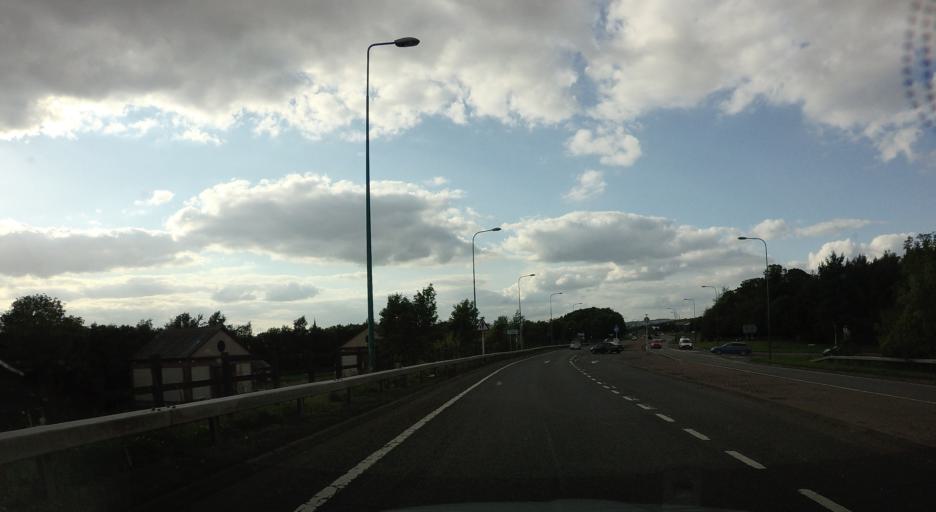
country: GB
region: Scotland
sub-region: Angus
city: Muirhead
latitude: 56.4593
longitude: -3.0517
